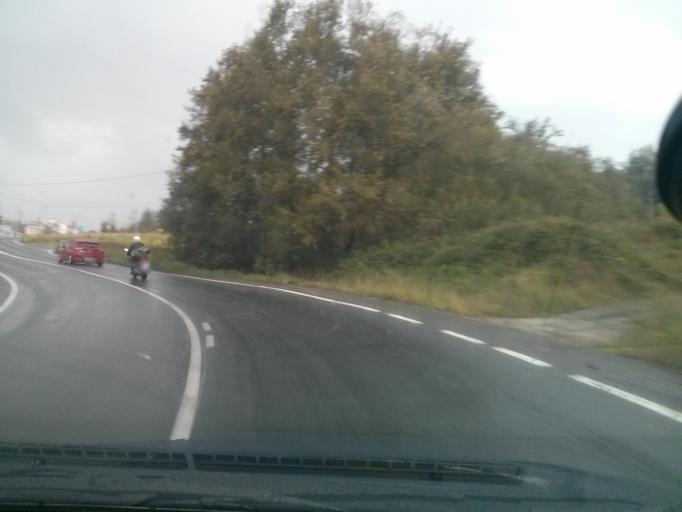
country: ES
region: Galicia
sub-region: Provincia da Coruna
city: Noia
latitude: 42.8028
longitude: -8.8837
